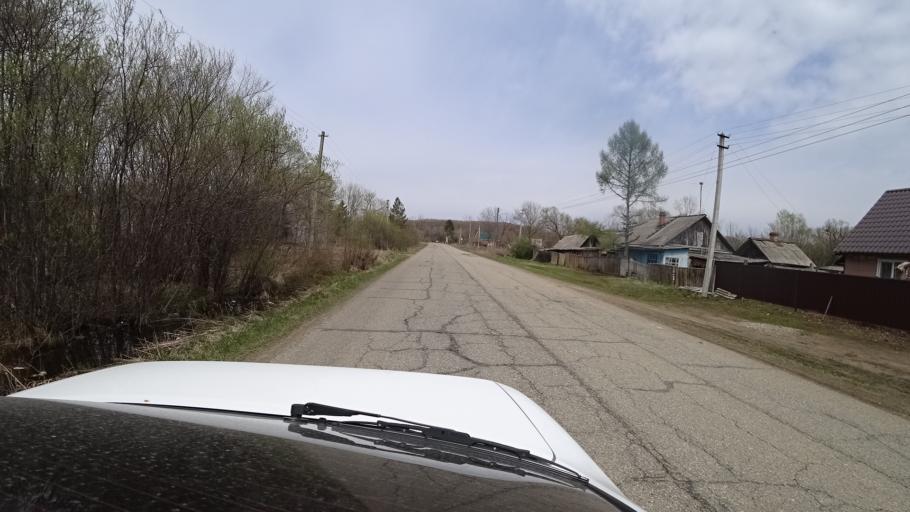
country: RU
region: Primorskiy
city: Novopokrovka
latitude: 45.7870
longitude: 134.1150
